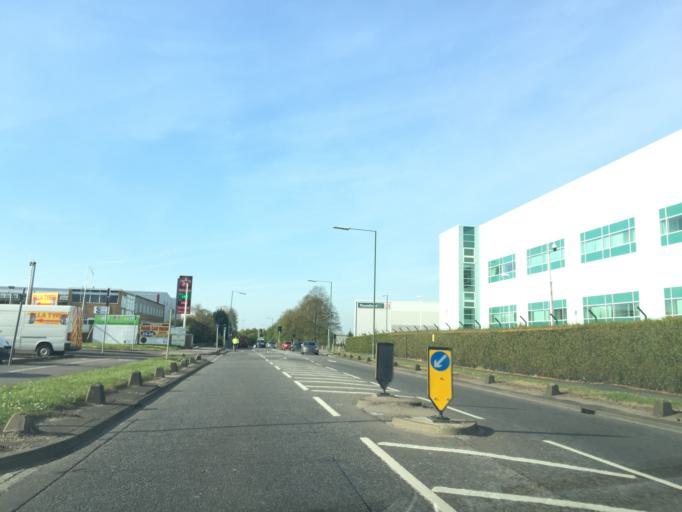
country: GB
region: England
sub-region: Essex
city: Roydon
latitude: 51.7666
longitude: 0.0678
